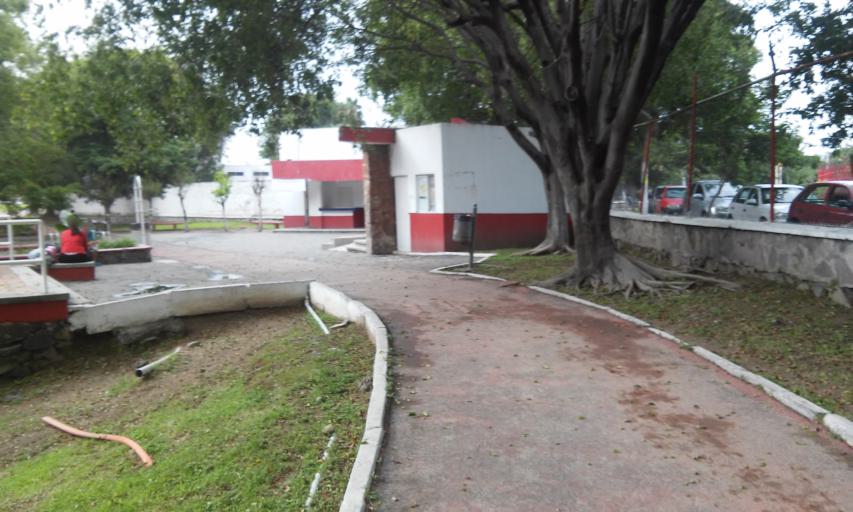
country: MX
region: Jalisco
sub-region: Zapopan
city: Zapopan
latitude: 20.7084
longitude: -103.3353
